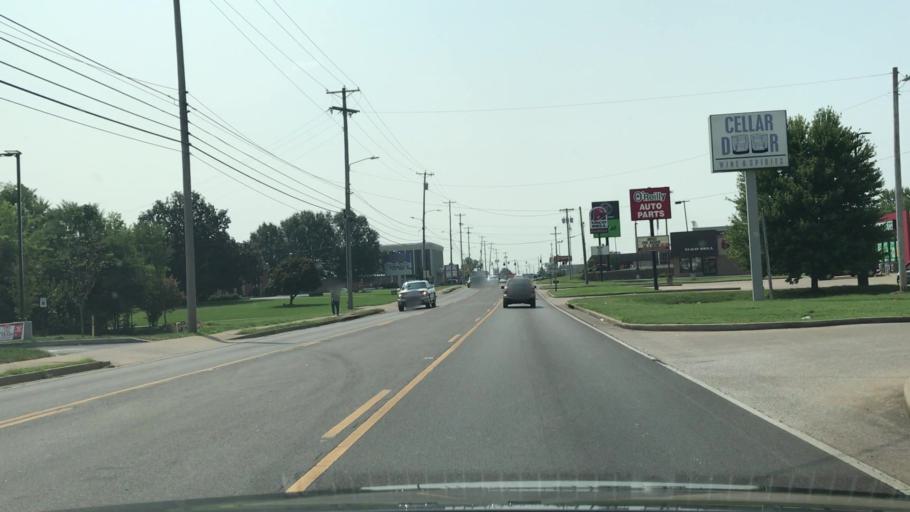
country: US
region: Kentucky
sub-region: Graves County
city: Mayfield
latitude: 36.7274
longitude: -88.6302
